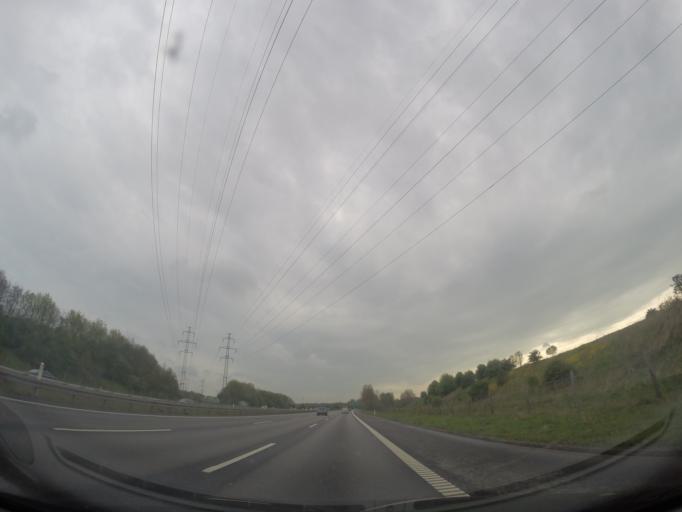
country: DK
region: Capital Region
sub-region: Hoje-Taastrup Kommune
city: Taastrup
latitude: 55.6730
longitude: 12.3210
